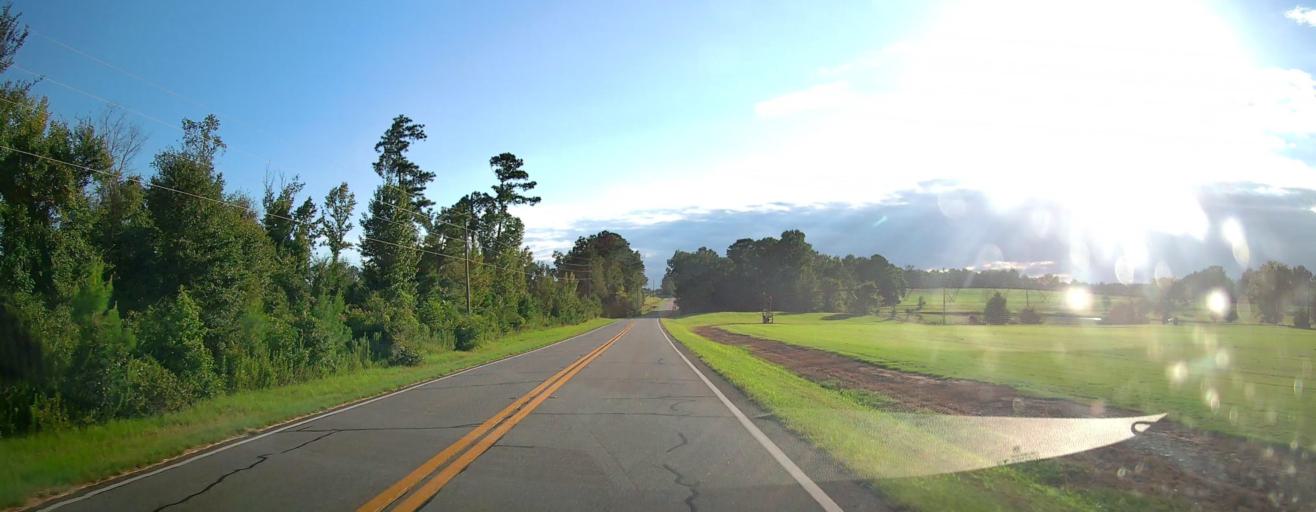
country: US
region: Georgia
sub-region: Pulaski County
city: Hawkinsville
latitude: 32.2698
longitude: -83.5076
